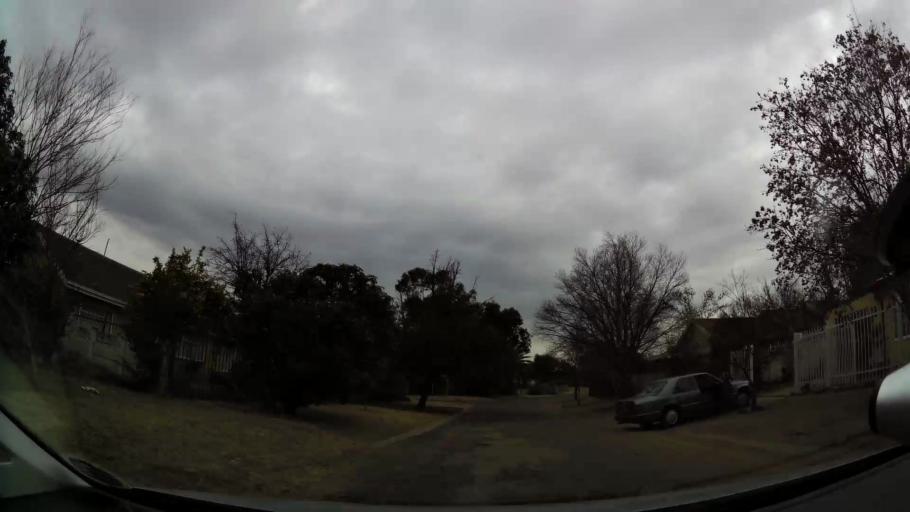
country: ZA
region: Orange Free State
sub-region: Fezile Dabi District Municipality
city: Kroonstad
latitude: -27.6507
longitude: 27.2462
